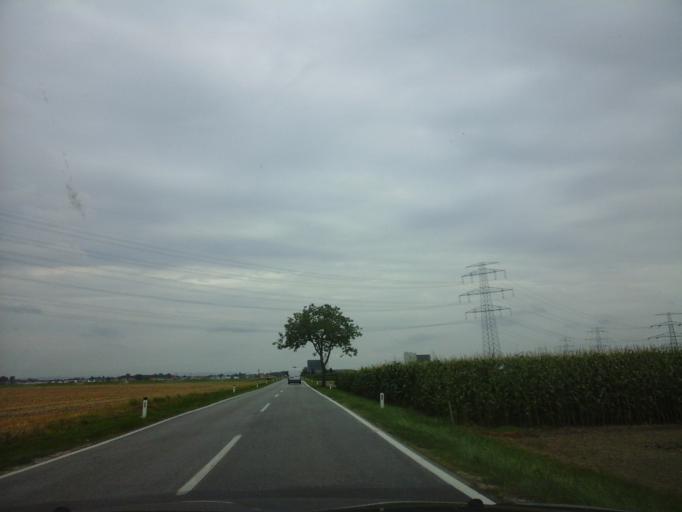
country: AT
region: Lower Austria
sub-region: Politischer Bezirk Ganserndorf
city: Mannsdorf an der Donau
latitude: 48.1618
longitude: 16.6391
